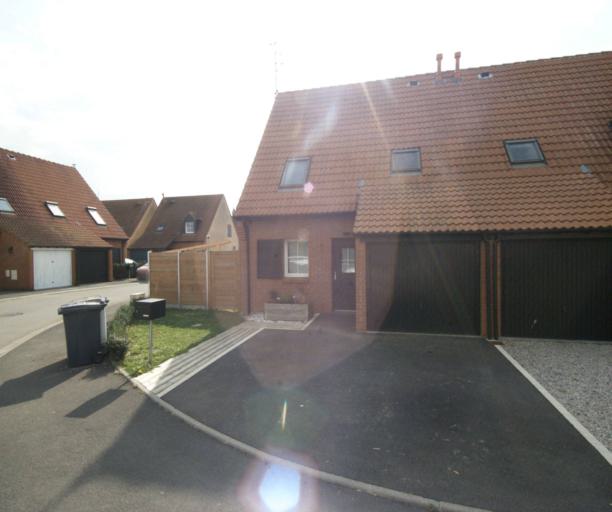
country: FR
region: Nord-Pas-de-Calais
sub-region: Departement du Nord
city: Don
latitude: 50.5451
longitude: 2.9200
